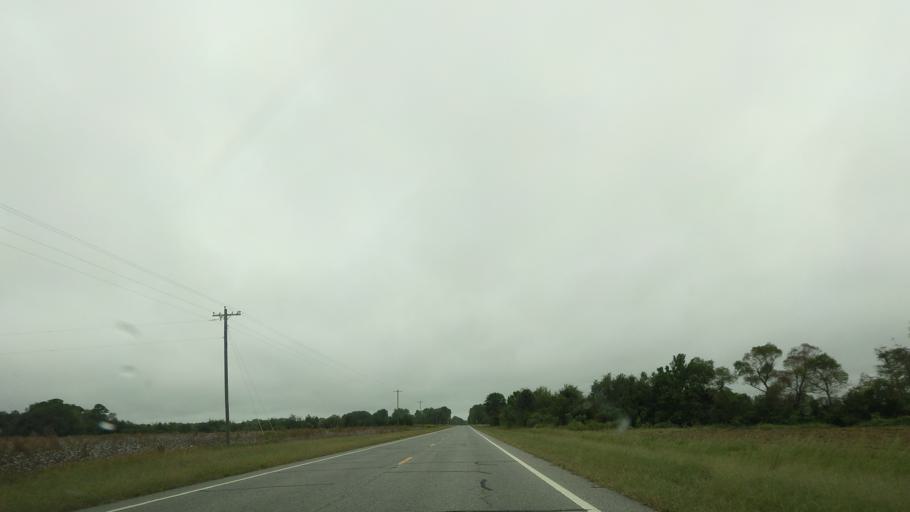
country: US
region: Georgia
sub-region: Berrien County
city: Enigma
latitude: 31.4778
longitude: -83.2377
